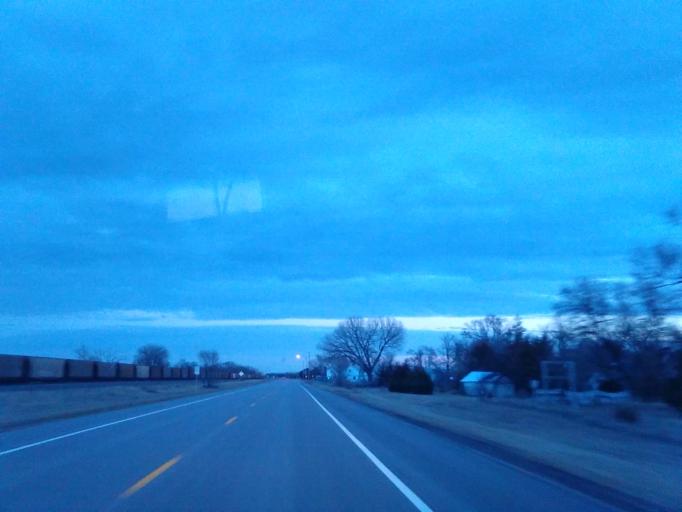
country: US
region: Nebraska
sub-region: Garden County
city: Oshkosh
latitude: 41.3309
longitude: -102.1400
